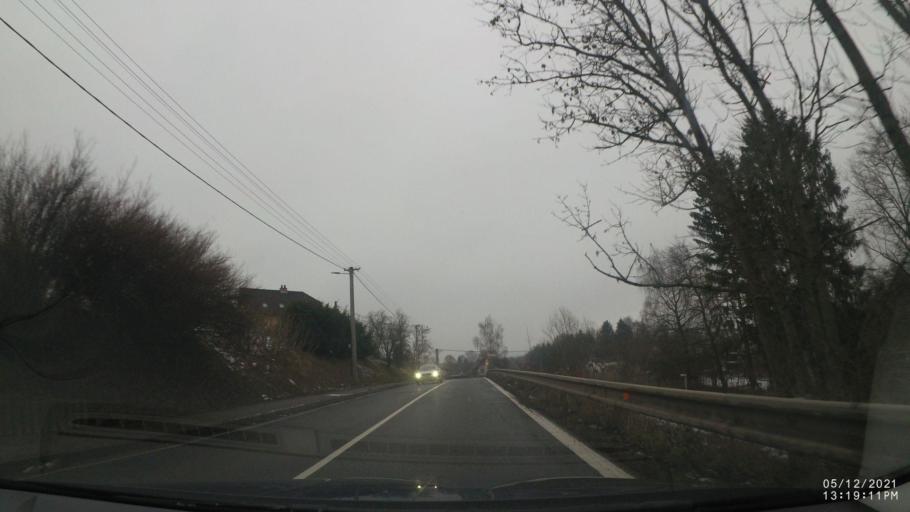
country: CZ
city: Velke Porici
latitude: 50.4405
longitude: 16.1927
